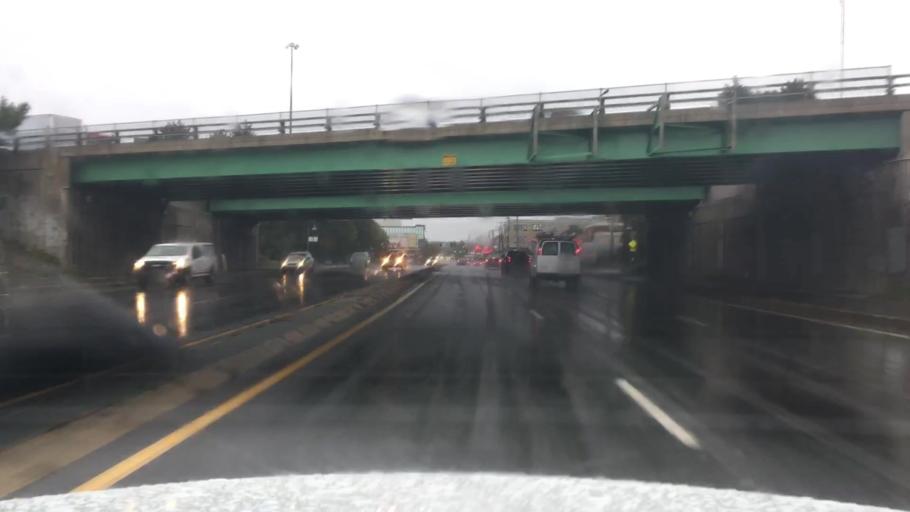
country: US
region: Maine
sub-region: Cumberland County
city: Portland
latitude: 43.6616
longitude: -70.2697
